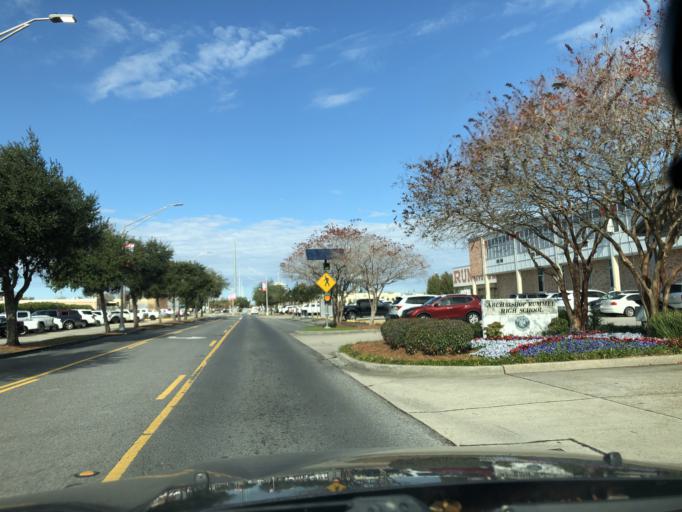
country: US
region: Louisiana
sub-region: Jefferson Parish
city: Metairie
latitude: 29.9900
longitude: -90.1600
